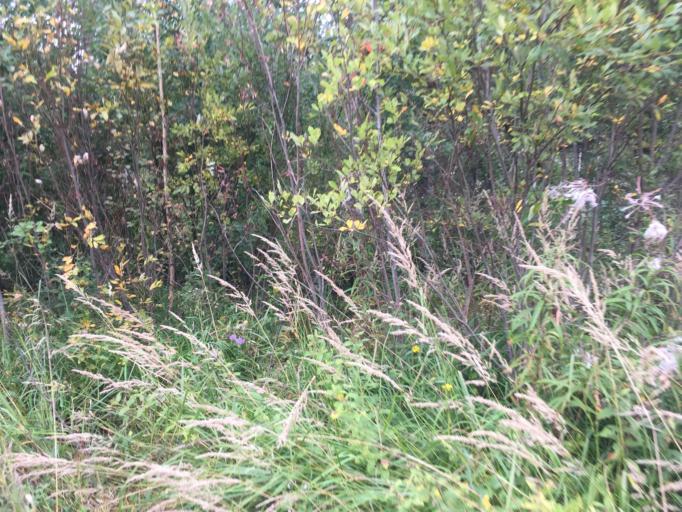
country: RU
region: Leningrad
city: Siverskiy
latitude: 59.3172
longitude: 30.0342
